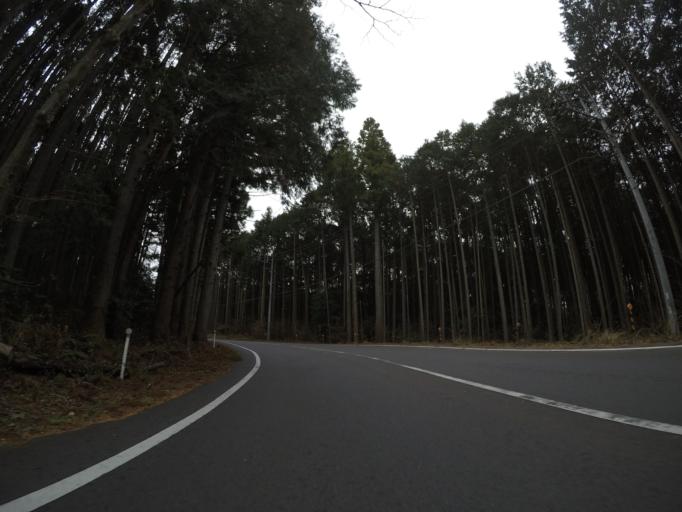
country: JP
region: Shizuoka
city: Fujinomiya
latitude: 35.2389
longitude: 138.5737
